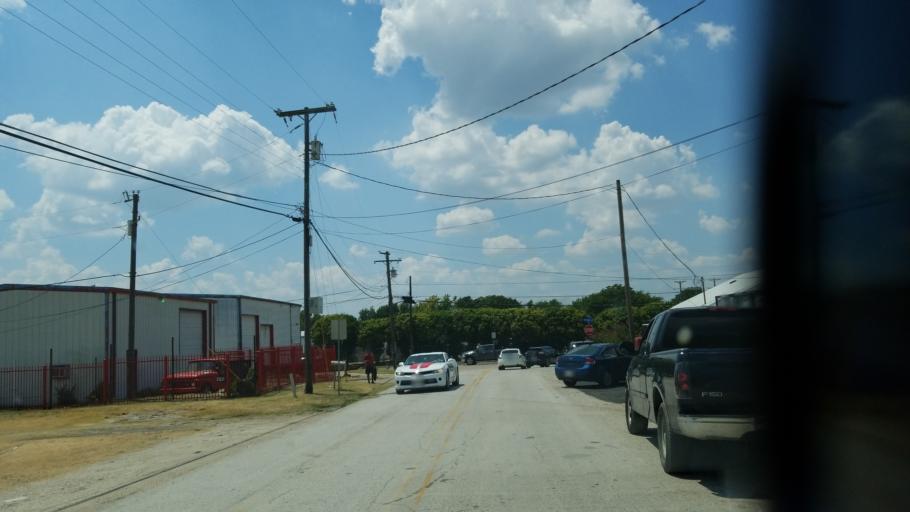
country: US
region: Texas
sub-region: Dallas County
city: Duncanville
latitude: 32.6742
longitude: -96.9032
